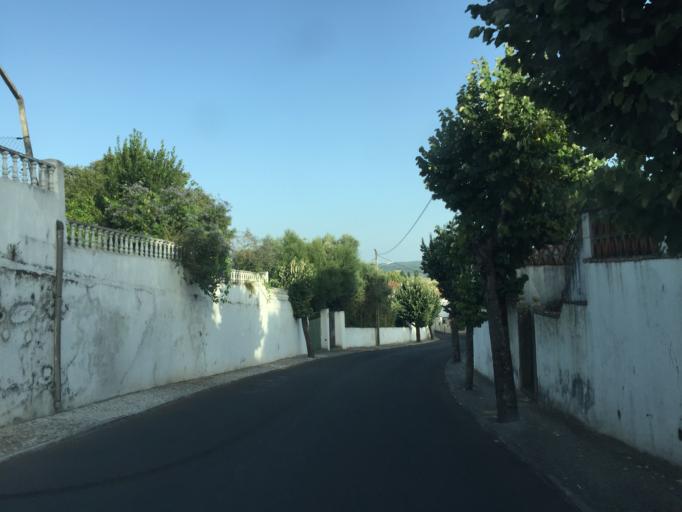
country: PT
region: Santarem
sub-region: Chamusca
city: Vila Nova da Barquinha
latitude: 39.4606
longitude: -8.4347
